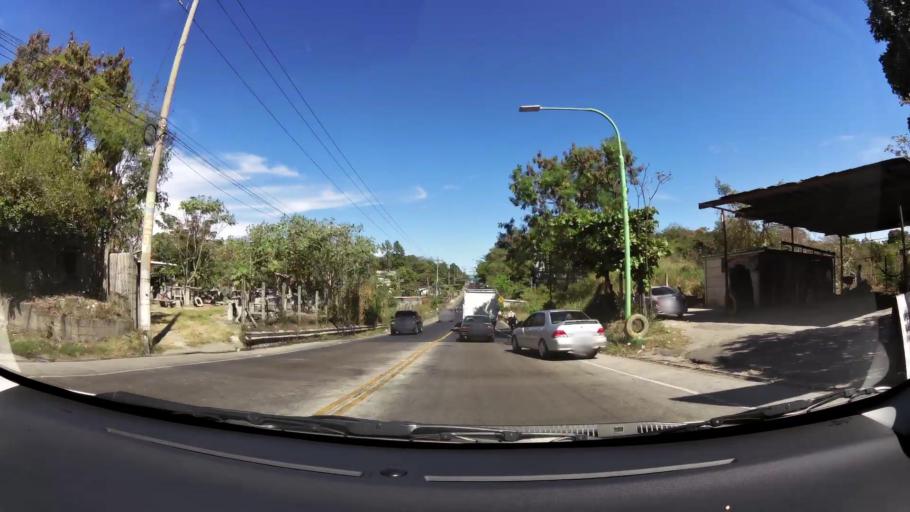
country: SV
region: San Salvador
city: Apopa
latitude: 13.8033
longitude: -89.1755
